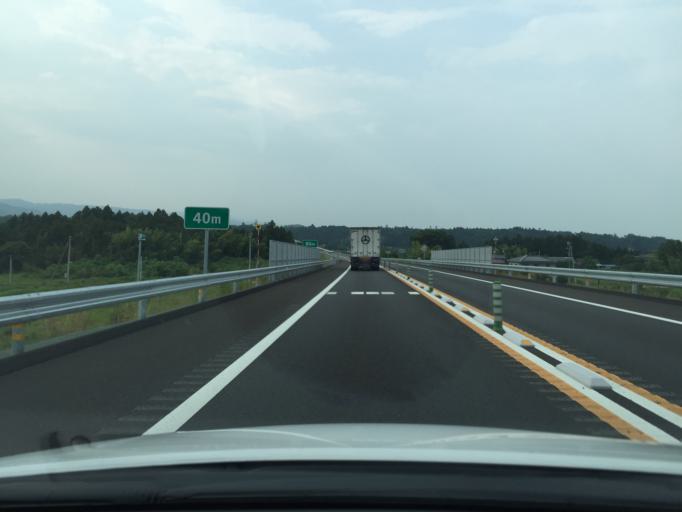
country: JP
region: Fukushima
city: Namie
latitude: 37.4701
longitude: 140.9619
